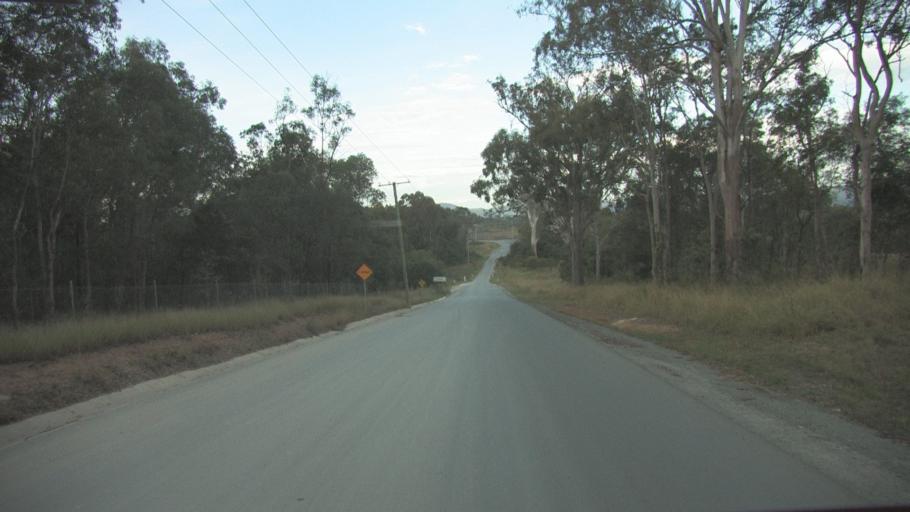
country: AU
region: Queensland
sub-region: Logan
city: Cedar Vale
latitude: -27.8573
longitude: 153.1170
